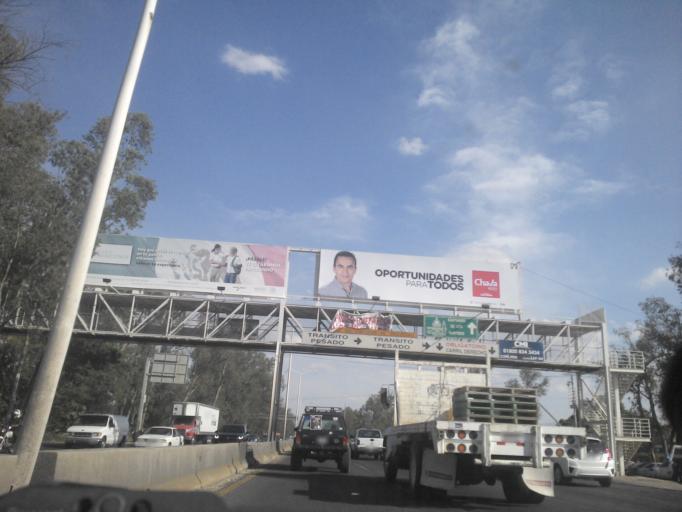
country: MX
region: Jalisco
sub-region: Tlajomulco de Zuniga
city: Palomar
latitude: 20.6261
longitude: -103.4341
